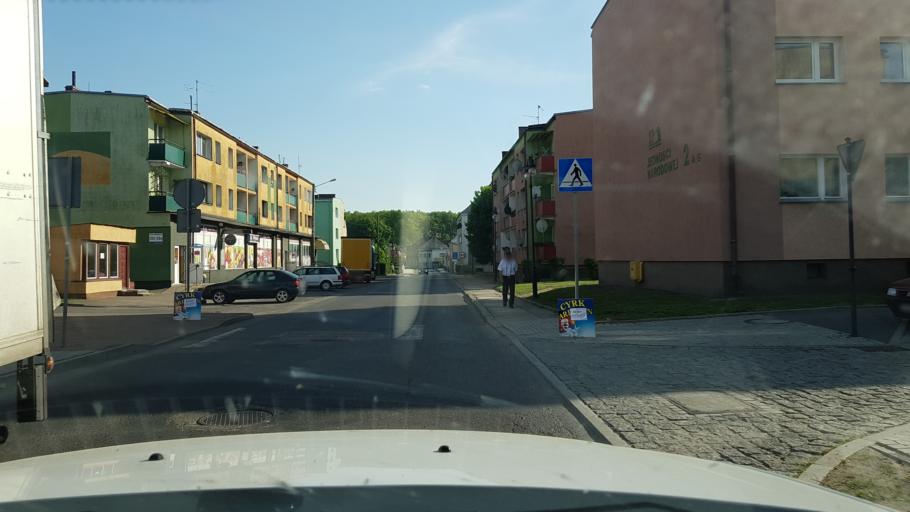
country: PL
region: West Pomeranian Voivodeship
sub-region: Powiat lobeski
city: Resko
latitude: 53.7728
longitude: 15.4046
